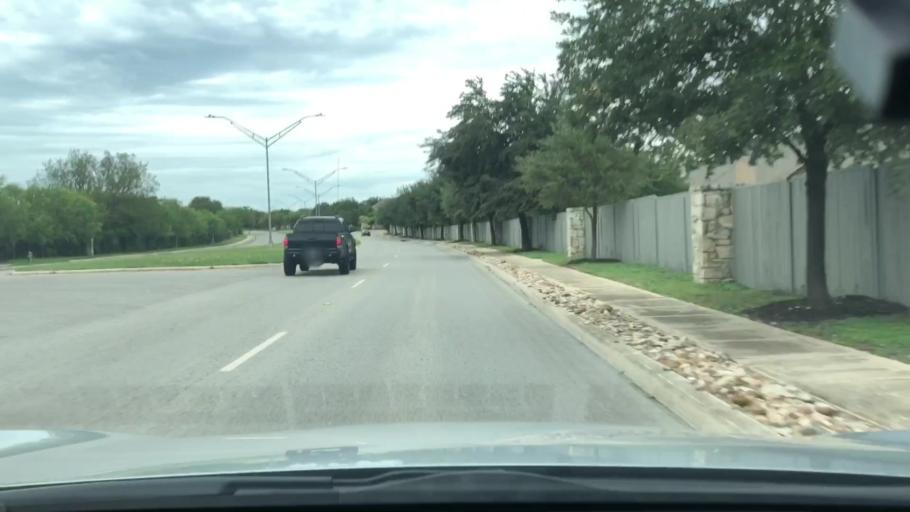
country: US
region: Texas
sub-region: Bexar County
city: Leon Valley
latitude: 29.4514
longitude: -98.6686
